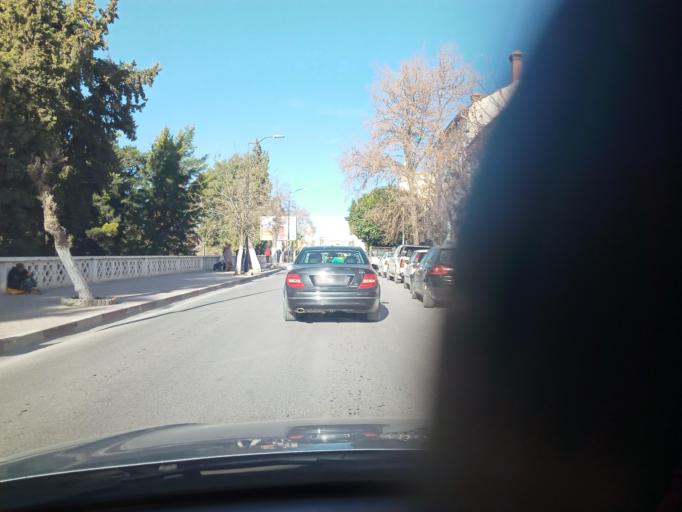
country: TN
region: Kef
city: El Kef
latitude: 36.1794
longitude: 8.7124
